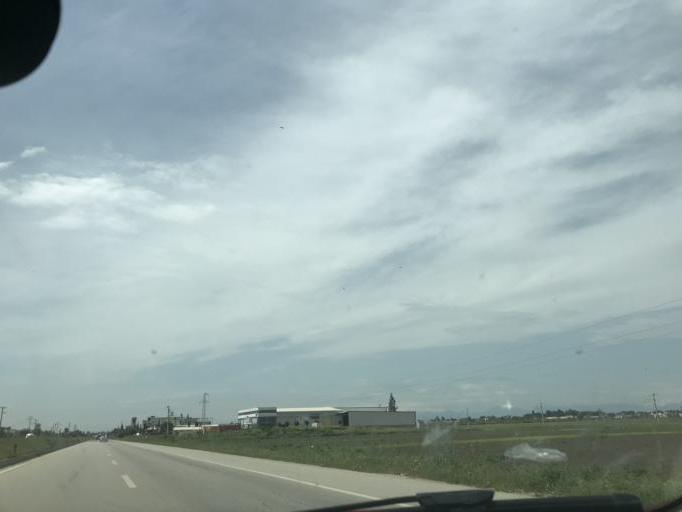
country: TR
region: Adana
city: Yuregir
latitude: 36.9797
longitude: 35.4546
